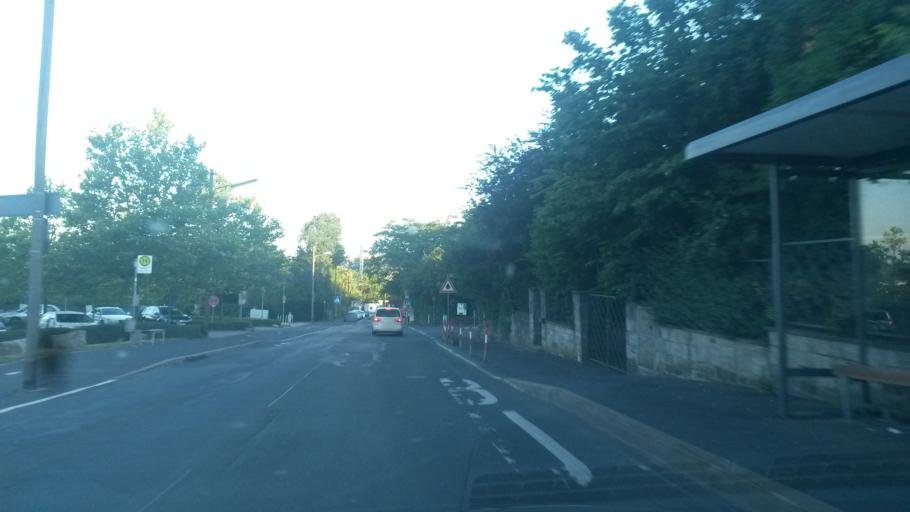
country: DE
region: Bavaria
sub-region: Regierungsbezirk Unterfranken
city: Wuerzburg
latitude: 49.8059
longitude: 9.9571
